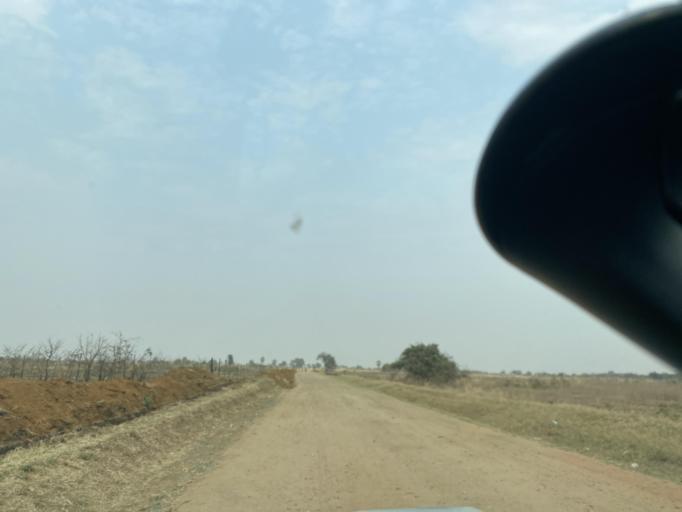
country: ZM
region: Lusaka
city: Kafue
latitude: -15.6450
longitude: 28.0824
